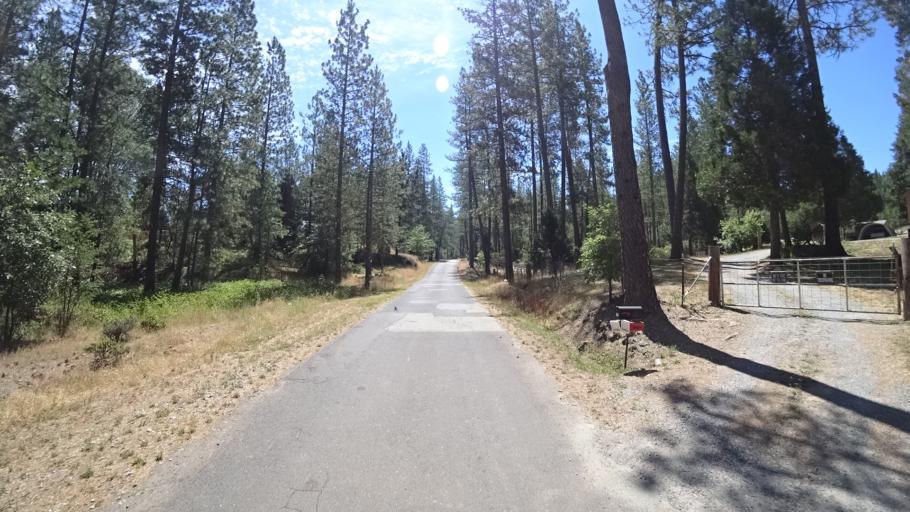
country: US
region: California
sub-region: Amador County
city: Pioneer
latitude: 38.3391
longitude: -120.5083
